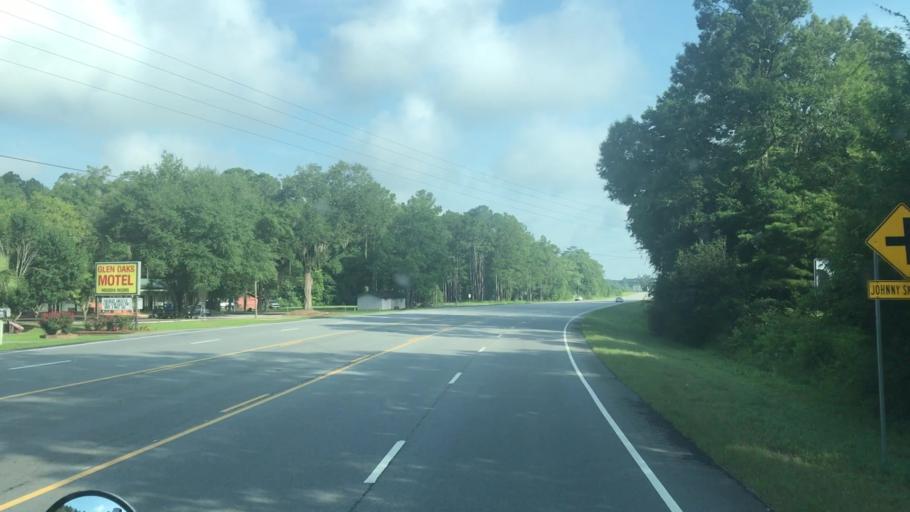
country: US
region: Georgia
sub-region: Decatur County
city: Bainbridge
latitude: 30.8708
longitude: -84.5609
